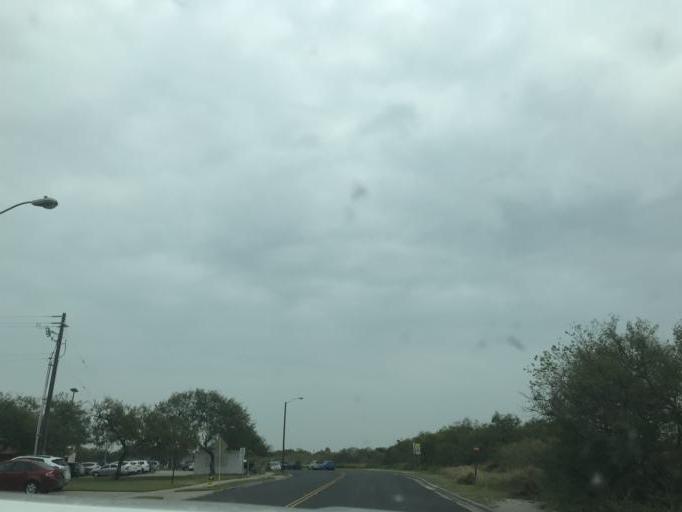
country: US
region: Texas
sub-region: Nueces County
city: Corpus Christi
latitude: 27.6683
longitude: -97.3493
